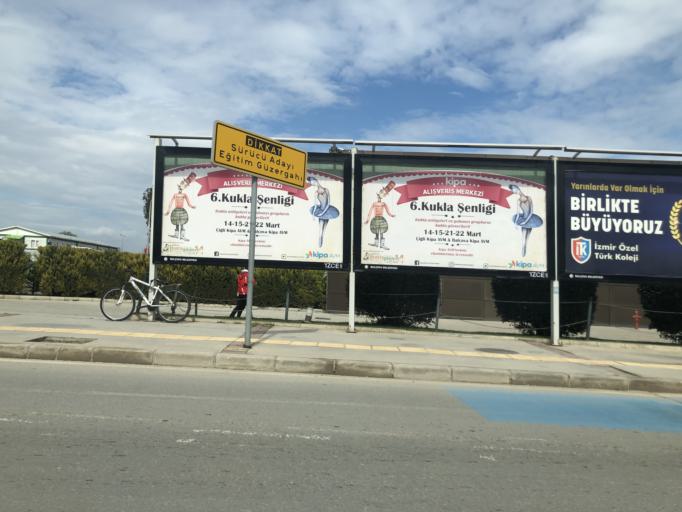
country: TR
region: Izmir
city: Karsiyaka
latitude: 38.3944
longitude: 27.0479
